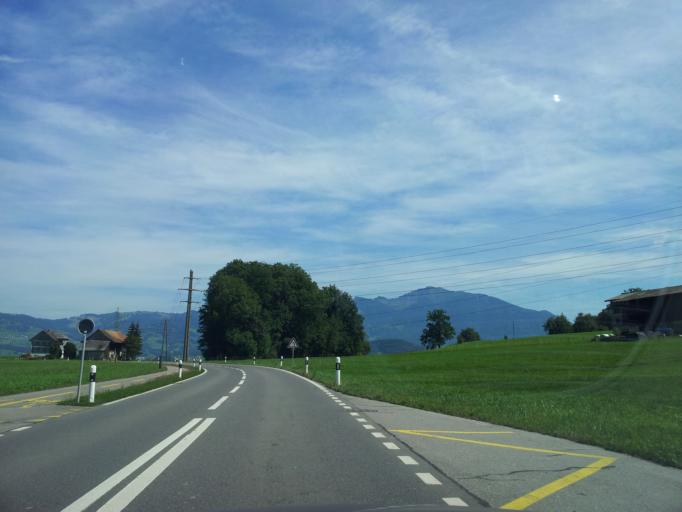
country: CH
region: Schwyz
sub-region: Bezirk March
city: Tuggen
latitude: 47.1919
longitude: 8.9339
